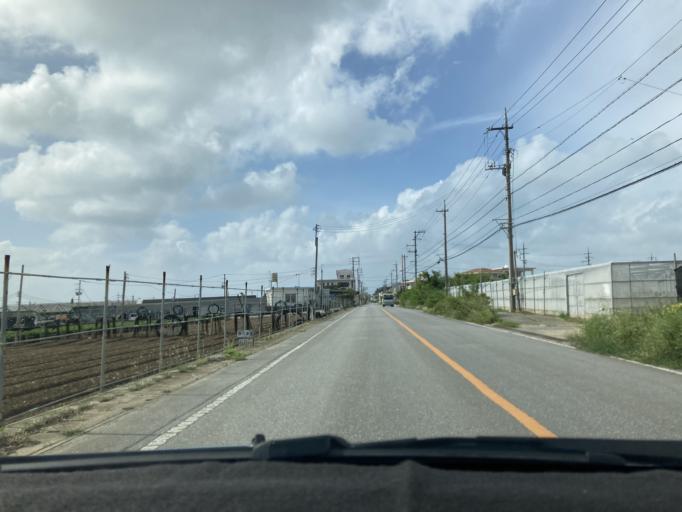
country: JP
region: Okinawa
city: Itoman
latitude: 26.1026
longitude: 127.6704
